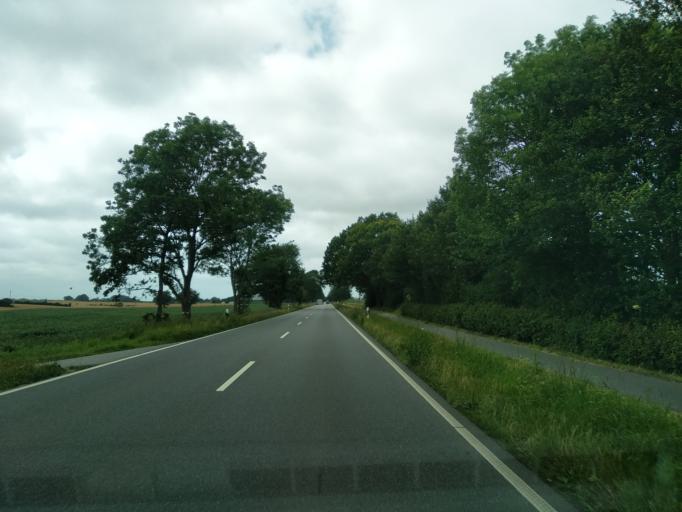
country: DE
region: Schleswig-Holstein
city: Langballig
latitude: 54.8002
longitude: 9.6209
